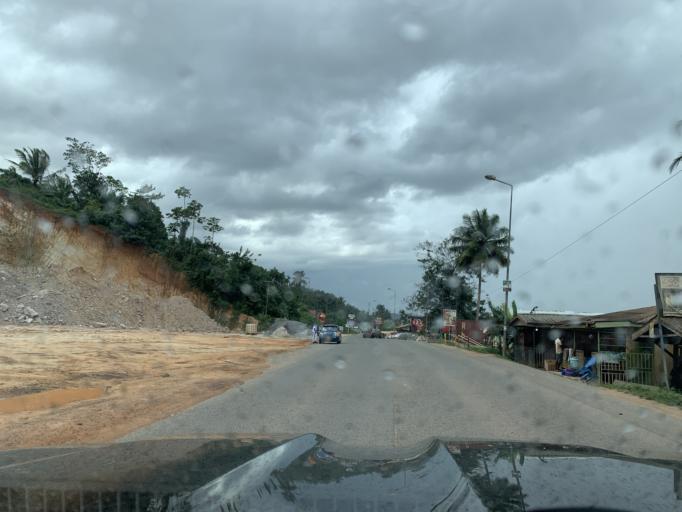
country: GH
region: Western
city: Tarkwa
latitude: 5.3168
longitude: -1.9892
